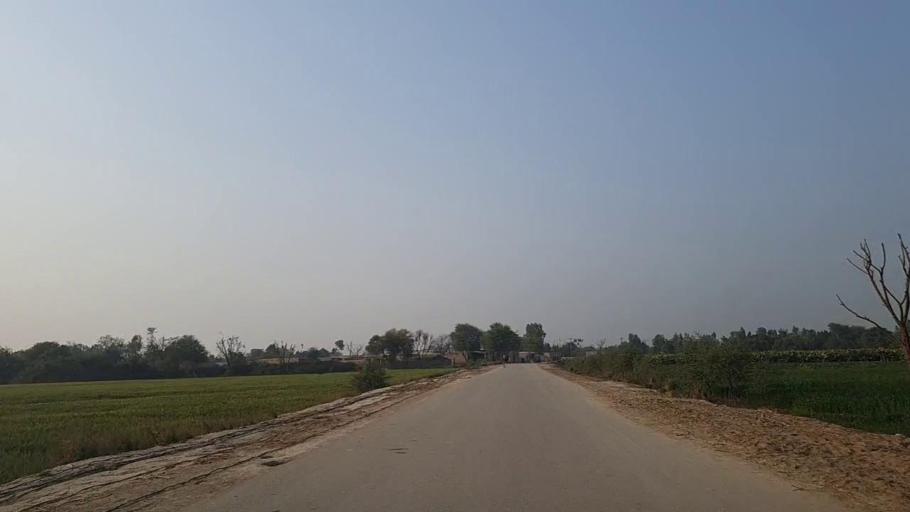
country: PK
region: Sindh
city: Sann
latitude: 26.1220
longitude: 68.1476
